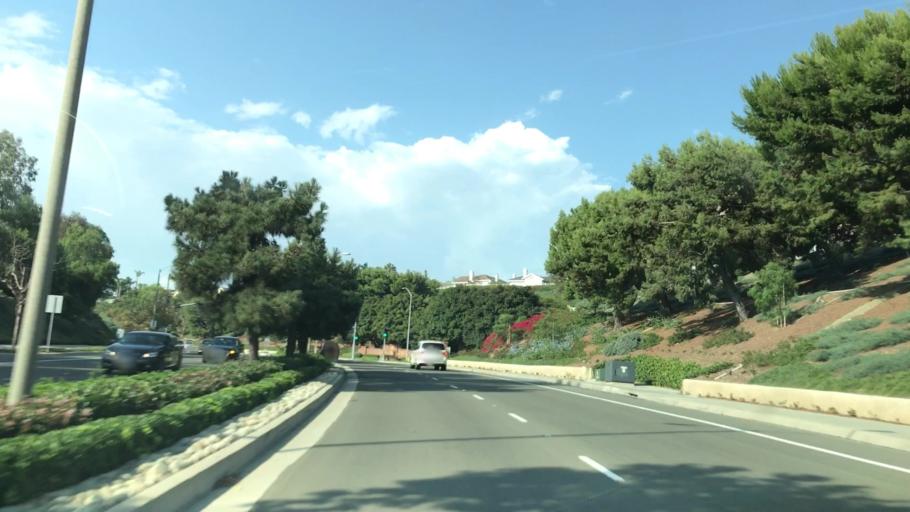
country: US
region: California
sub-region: Orange County
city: Dana Point
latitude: 33.4915
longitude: -117.7097
